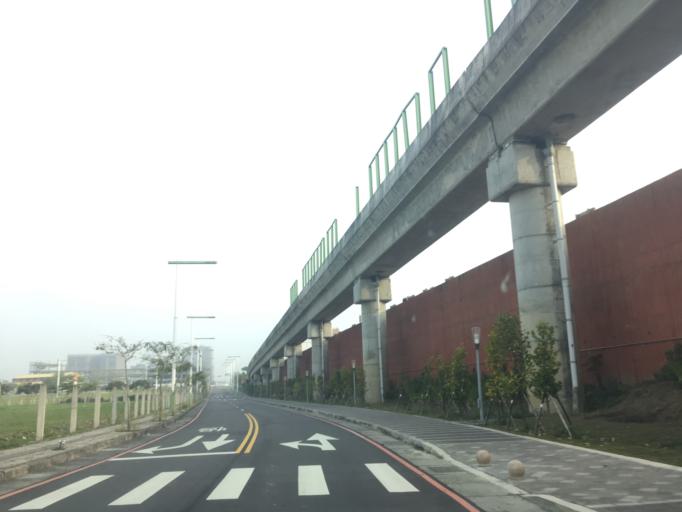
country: TW
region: Taiwan
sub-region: Taichung City
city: Taichung
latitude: 24.1838
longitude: 120.7101
